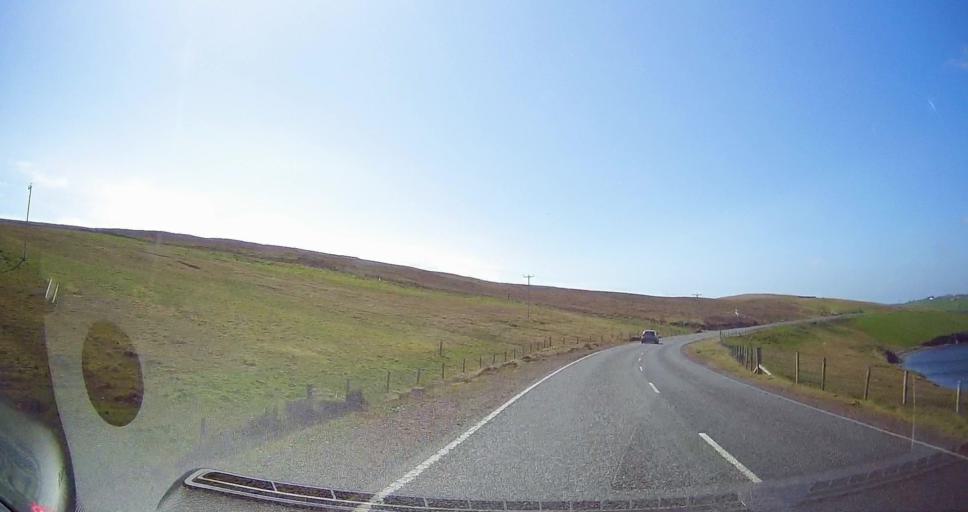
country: GB
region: Scotland
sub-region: Shetland Islands
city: Sandwick
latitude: 60.1098
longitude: -1.2965
